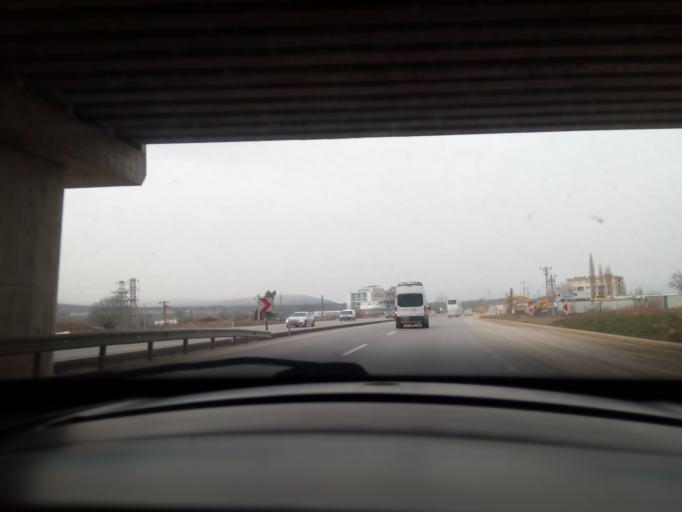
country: TR
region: Bursa
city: Tatkavakli
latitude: 40.0336
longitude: 28.3720
